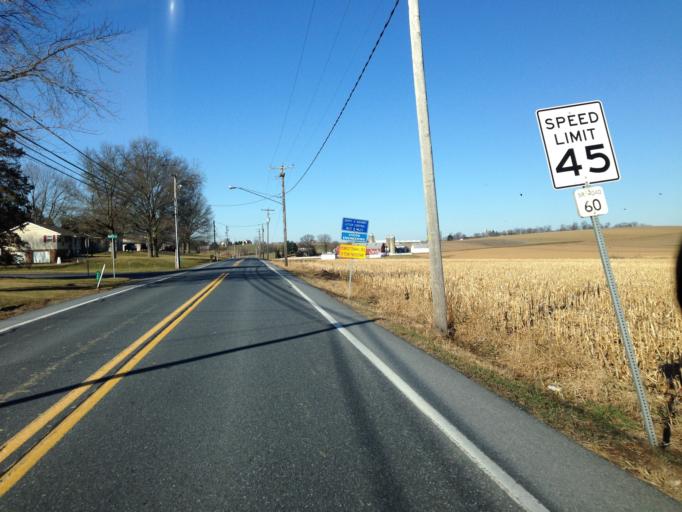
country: US
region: Pennsylvania
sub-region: Lancaster County
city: Penryn
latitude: 40.1784
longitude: -76.3509
